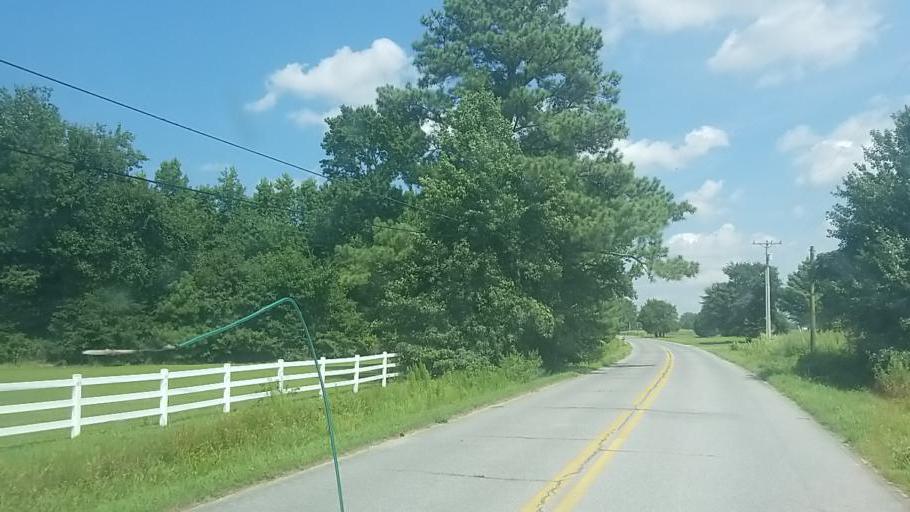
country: US
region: Maryland
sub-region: Wicomico County
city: Hebron
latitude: 38.4601
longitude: -75.7726
